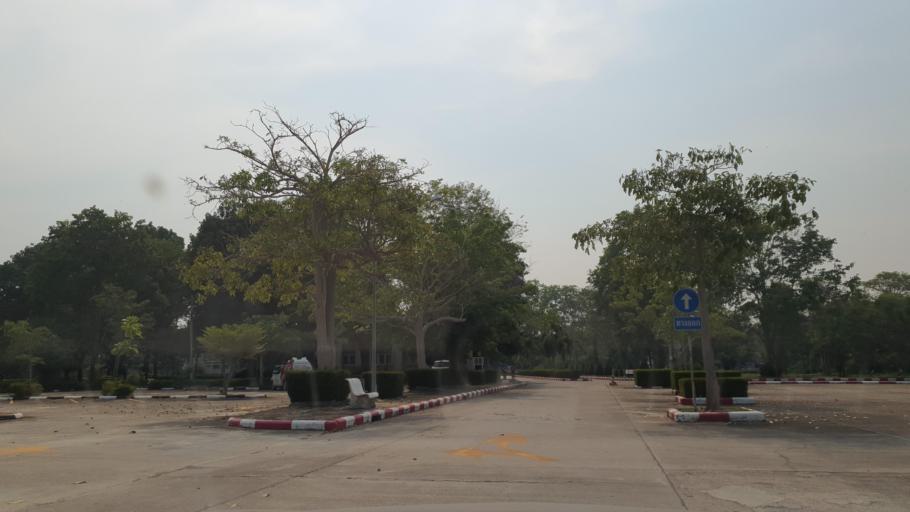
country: TH
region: Rayong
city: Rayong
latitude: 12.6102
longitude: 101.4240
